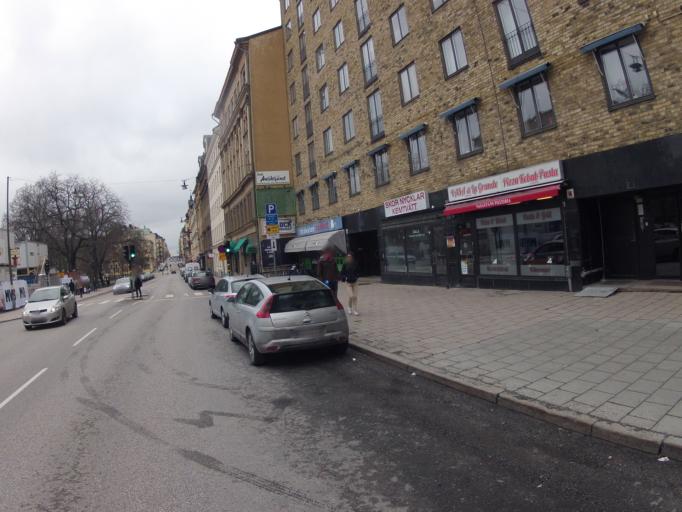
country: SE
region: Stockholm
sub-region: Stockholms Kommun
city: Stockholm
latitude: 59.3401
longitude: 18.0473
